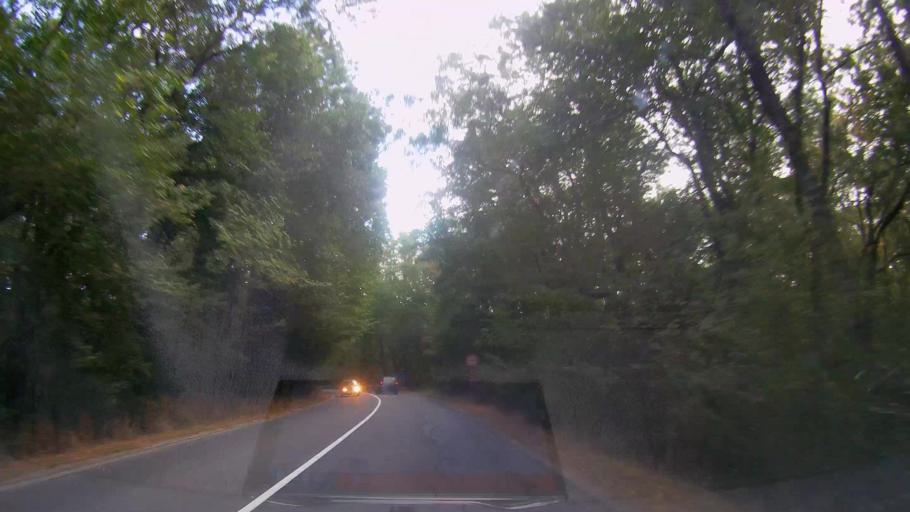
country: BG
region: Burgas
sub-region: Obshtina Primorsko
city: Primorsko
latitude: 42.3026
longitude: 27.7259
